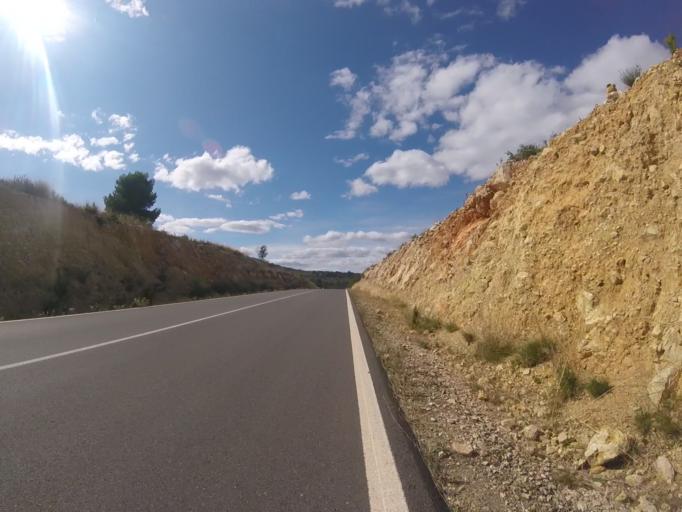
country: ES
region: Valencia
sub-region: Provincia de Castello
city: Chert/Xert
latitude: 40.4384
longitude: 0.1200
